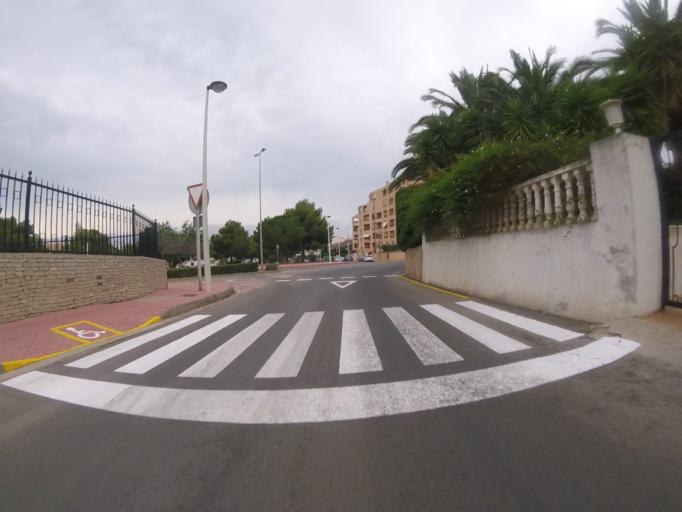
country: ES
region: Valencia
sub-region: Provincia de Castello
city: Alcoceber
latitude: 40.2570
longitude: 0.2887
